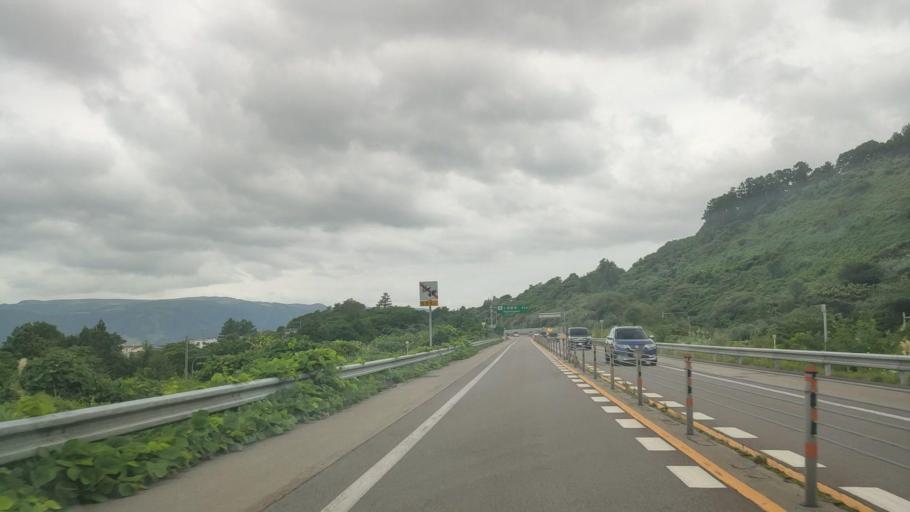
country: JP
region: Hokkaido
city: Nanae
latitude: 41.9120
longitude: 140.6922
